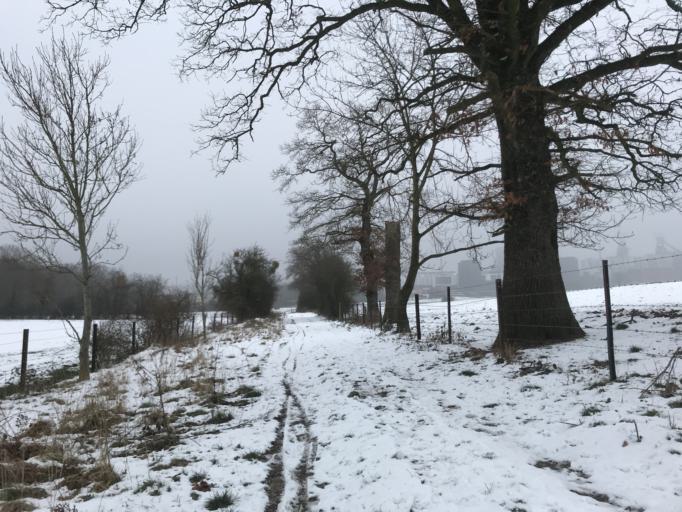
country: LU
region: Luxembourg
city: Belvaux
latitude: 49.4981
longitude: 5.9324
